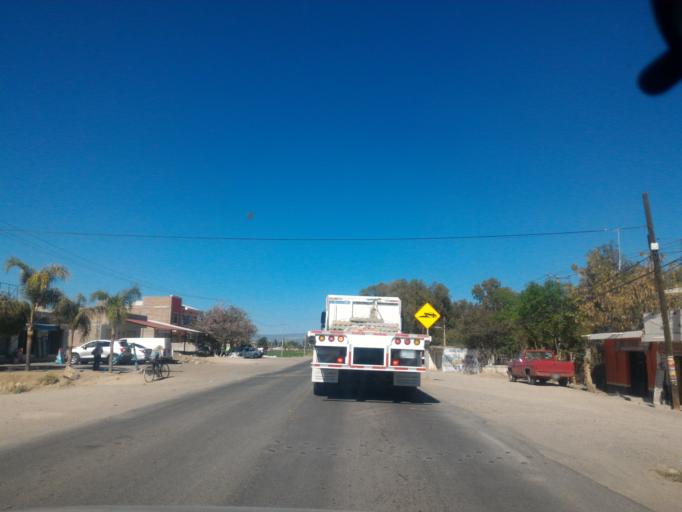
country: MX
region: Guanajuato
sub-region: Leon
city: Malagana (San Antonio del Monte)
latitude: 21.0396
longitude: -101.7684
